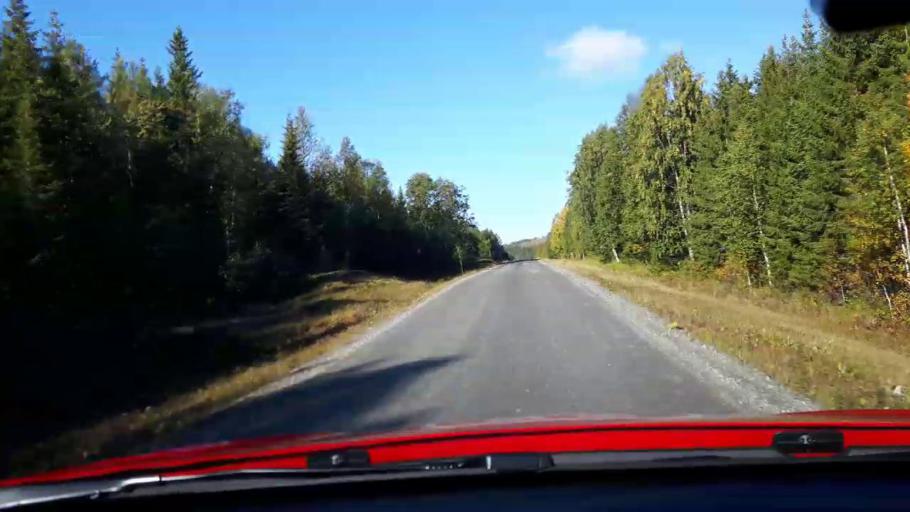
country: NO
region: Nord-Trondelag
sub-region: Lierne
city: Sandvika
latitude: 64.5868
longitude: 13.8741
